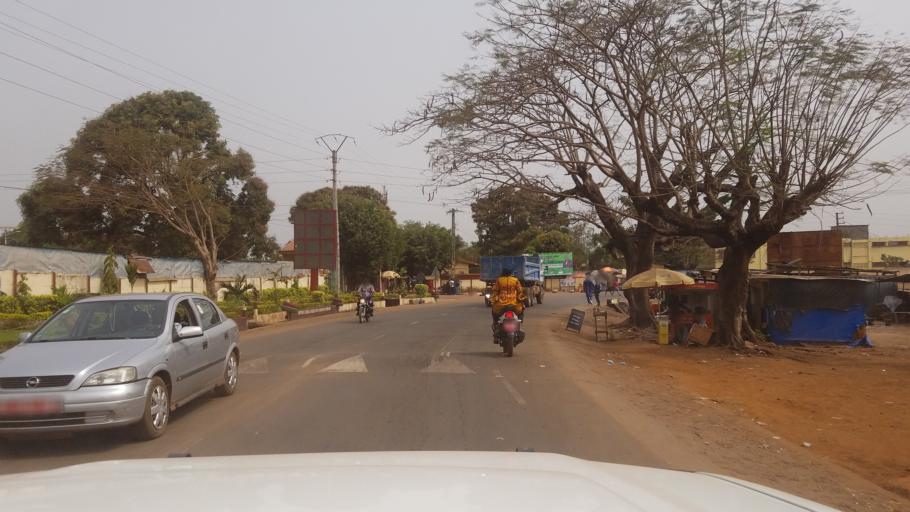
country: GN
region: Kindia
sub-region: Prefecture de Dubreka
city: Dubreka
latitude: 9.6799
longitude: -13.5802
